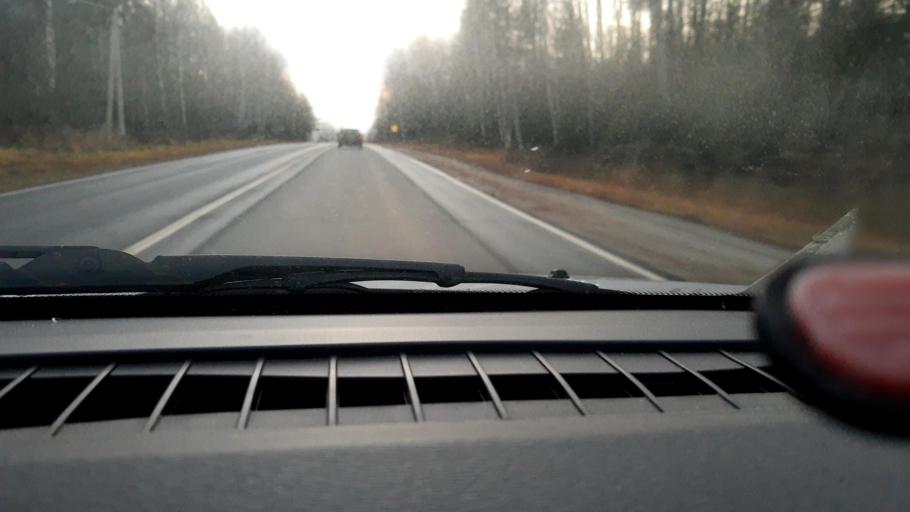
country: RU
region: Nizjnij Novgorod
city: Krasnyye Baki
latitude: 57.1029
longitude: 45.1826
